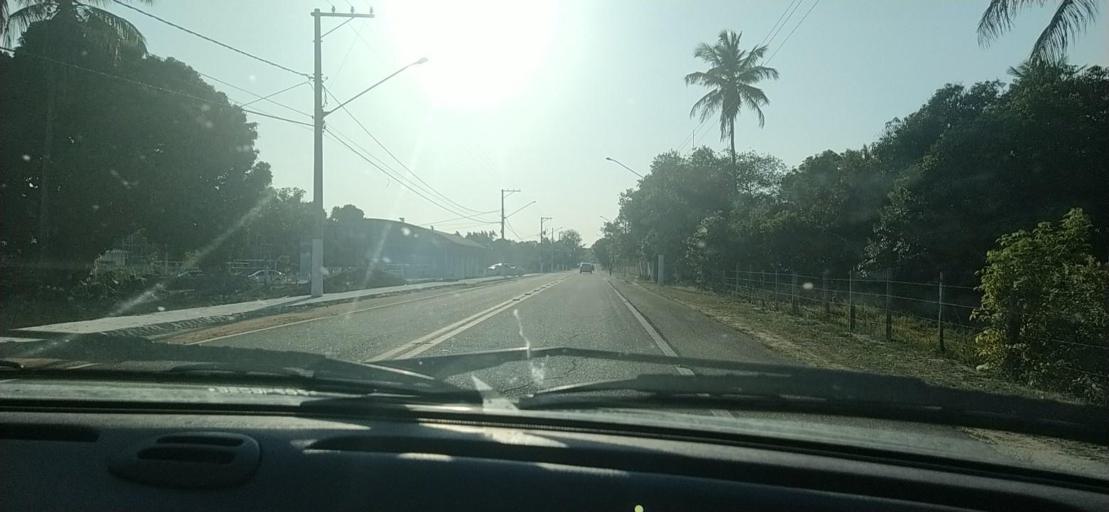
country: BR
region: Espirito Santo
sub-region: Conceicao Da Barra
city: Conceicao da Barra
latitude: -18.5675
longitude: -39.7553
